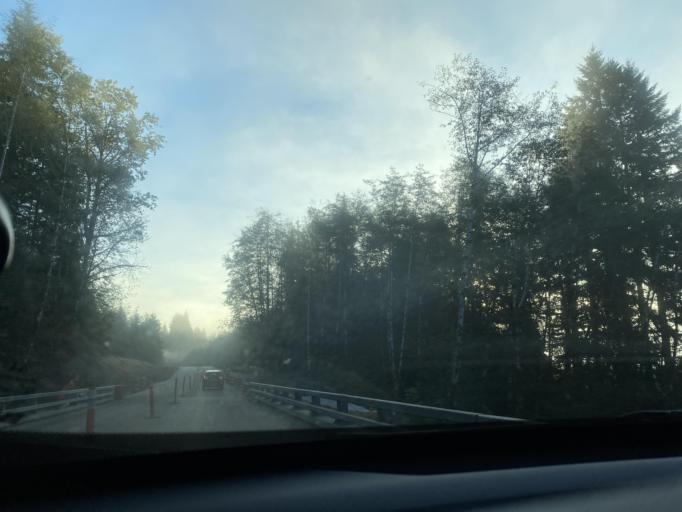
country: US
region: Washington
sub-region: Clallam County
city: Forks
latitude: 47.8135
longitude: -124.0712
